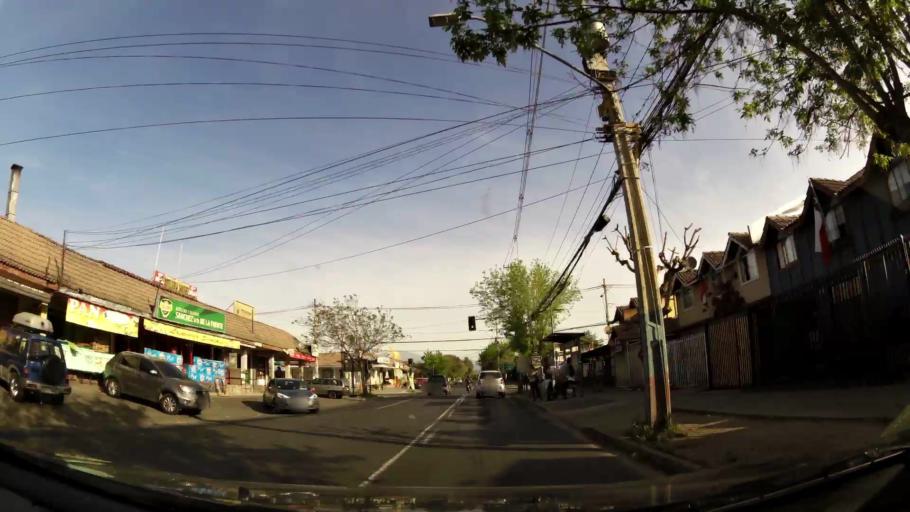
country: CL
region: Santiago Metropolitan
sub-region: Provincia de Cordillera
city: Puente Alto
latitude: -33.5852
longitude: -70.5683
